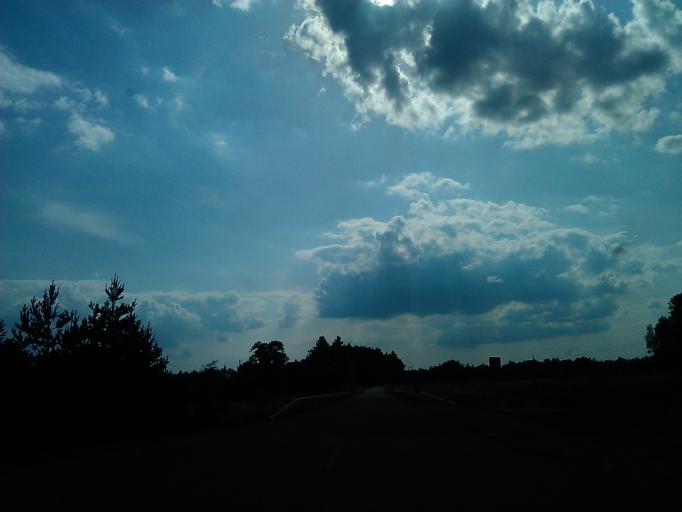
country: LV
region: Skrunda
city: Skrunda
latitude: 56.6813
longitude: 21.9306
